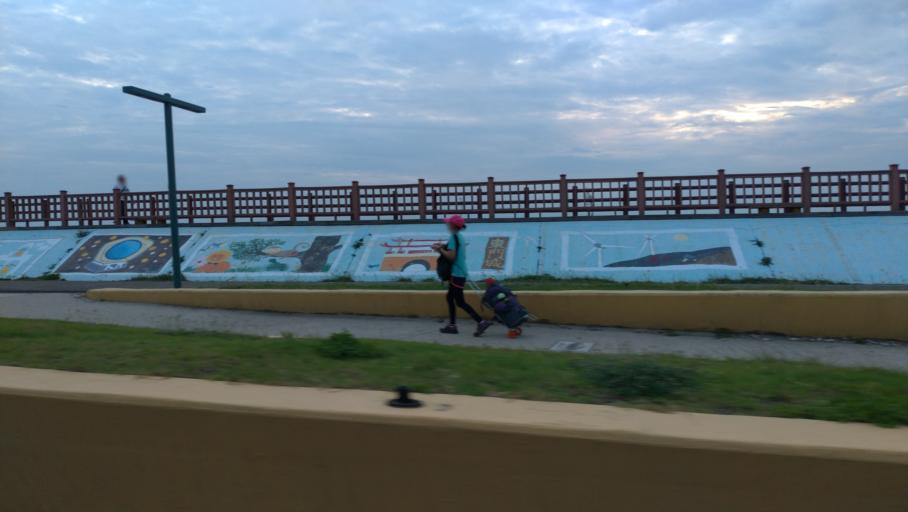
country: TW
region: Taiwan
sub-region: Hsinchu
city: Hsinchu
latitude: 24.7797
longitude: 120.9146
